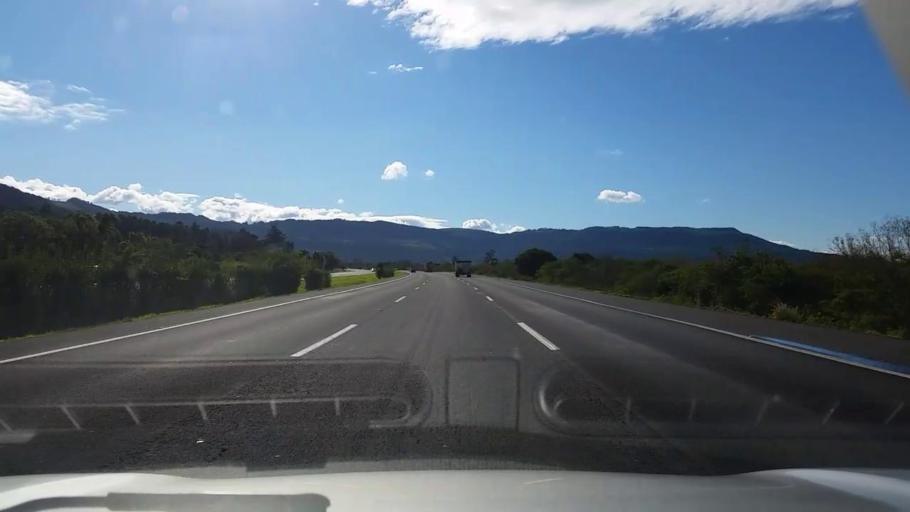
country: BR
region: Rio Grande do Sul
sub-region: Osorio
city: Osorio
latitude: -29.8816
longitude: -50.4357
